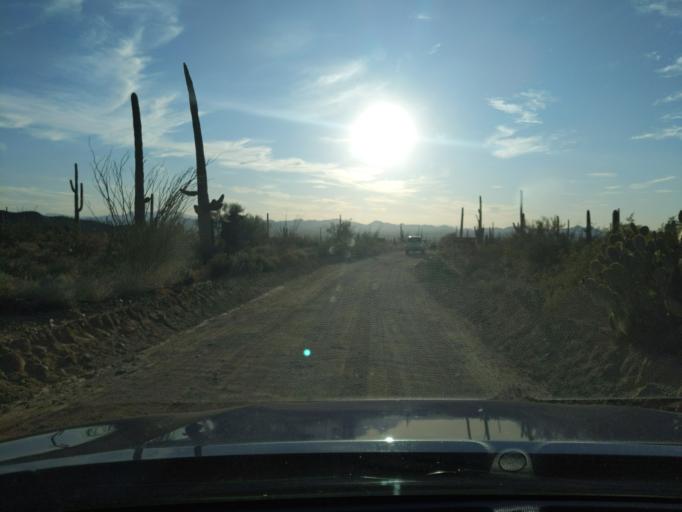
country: US
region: Arizona
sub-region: Pima County
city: Picture Rocks
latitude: 32.2876
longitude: -111.2020
